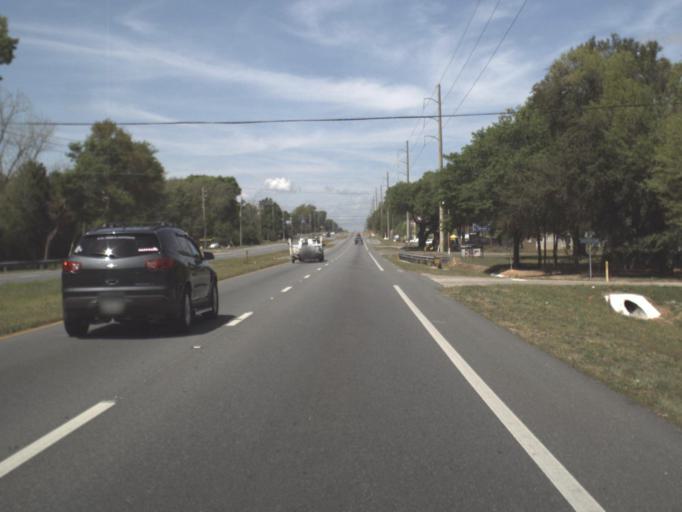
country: US
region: Florida
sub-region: Santa Rosa County
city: Milton
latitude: 30.6029
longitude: -87.0943
